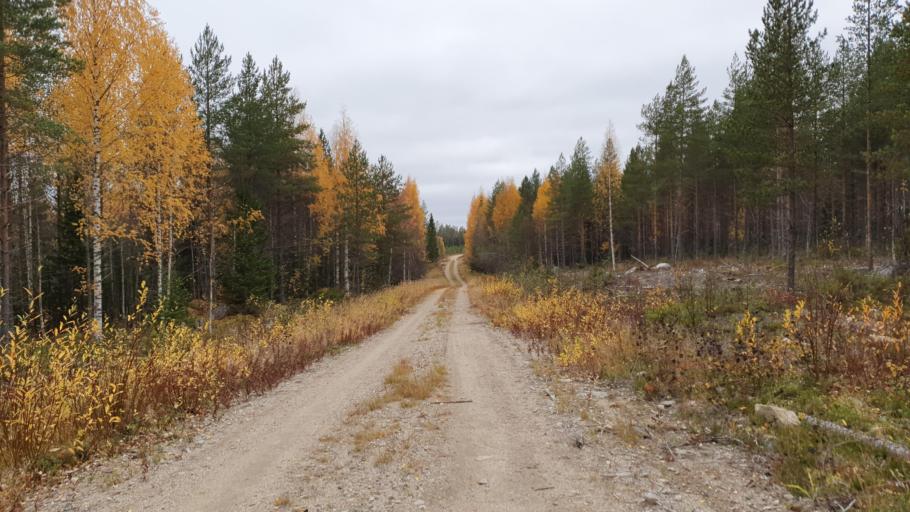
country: FI
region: Kainuu
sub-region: Kehys-Kainuu
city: Kuhmo
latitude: 64.4392
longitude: 29.6333
